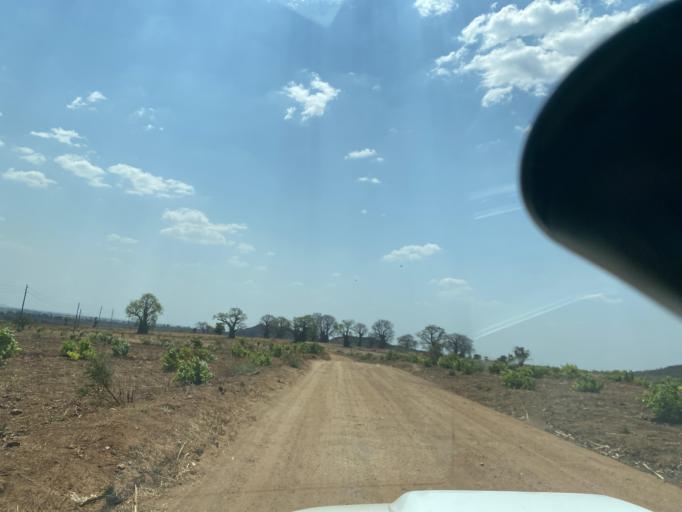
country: ZM
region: Southern
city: Nakambala
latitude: -15.5047
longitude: 27.9310
